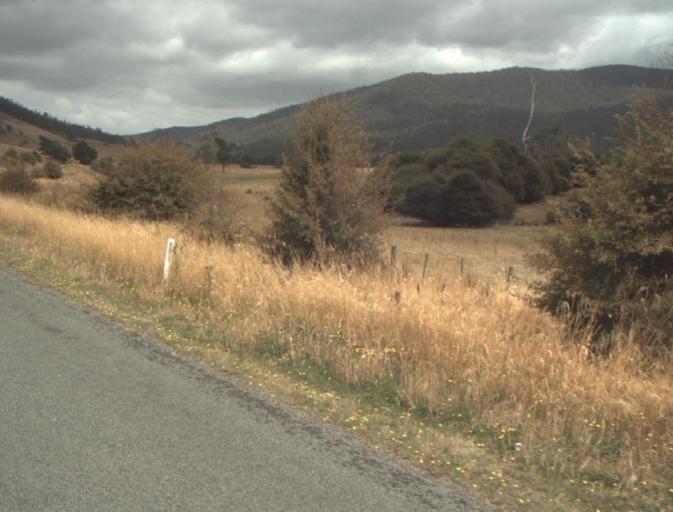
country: AU
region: Tasmania
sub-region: Northern Midlands
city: Evandale
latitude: -41.5007
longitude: 147.4690
